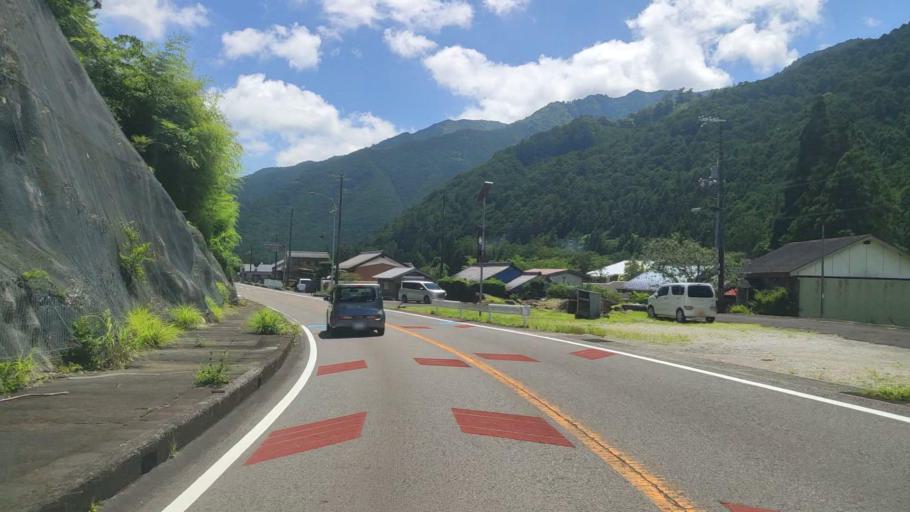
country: JP
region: Mie
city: Owase
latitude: 33.9803
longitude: 136.1051
